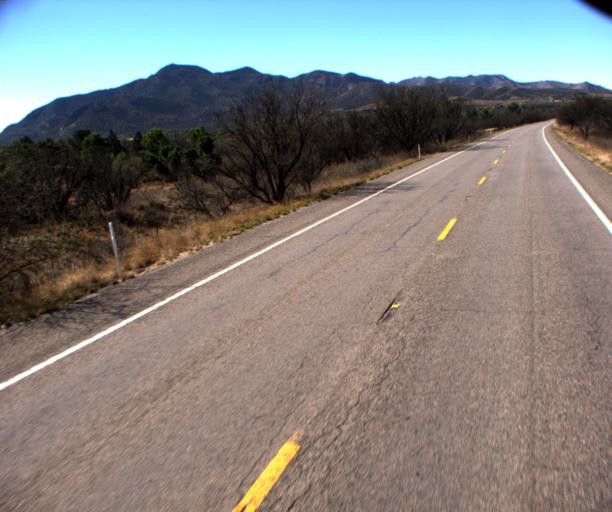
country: US
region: Arizona
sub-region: Santa Cruz County
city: Rio Rico
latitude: 31.5566
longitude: -110.7355
